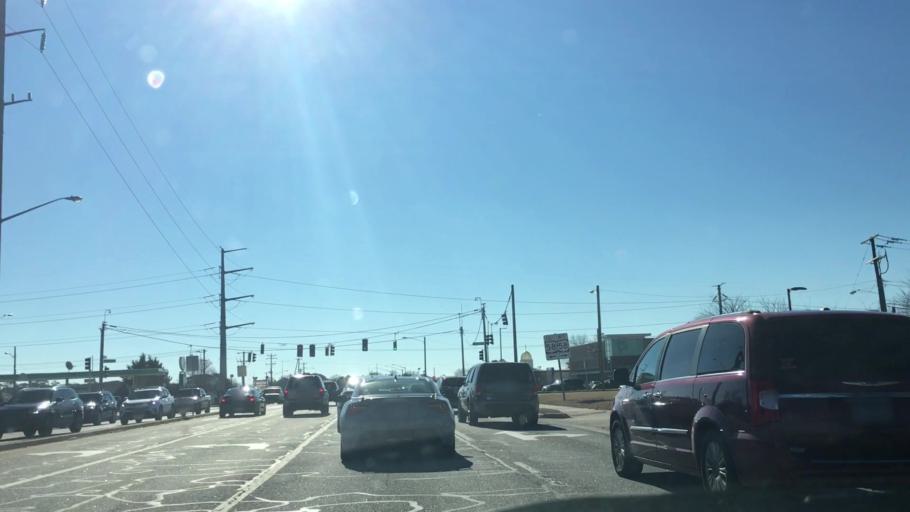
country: US
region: Virginia
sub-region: City of Virginia Beach
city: Virginia Beach
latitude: 36.8516
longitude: -76.0225
